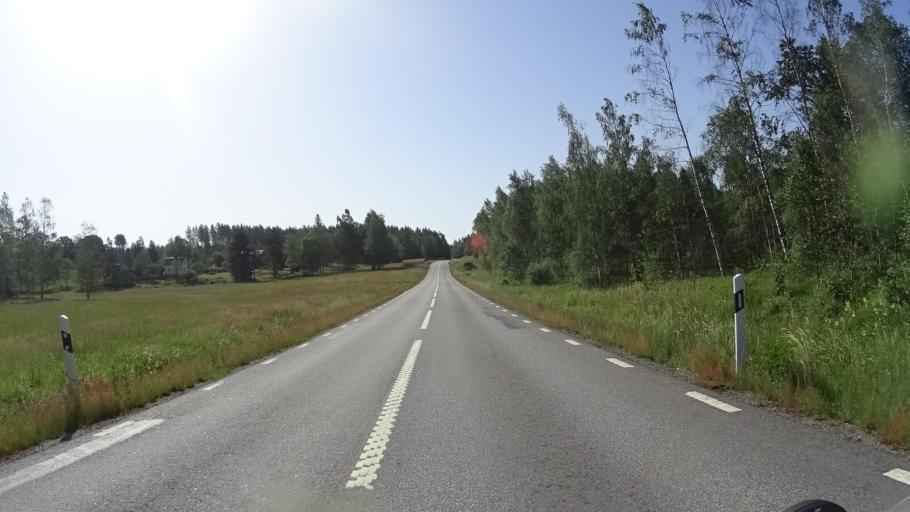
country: SE
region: OEstergoetland
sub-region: Atvidabergs Kommun
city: Atvidaberg
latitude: 58.0844
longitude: 16.1463
